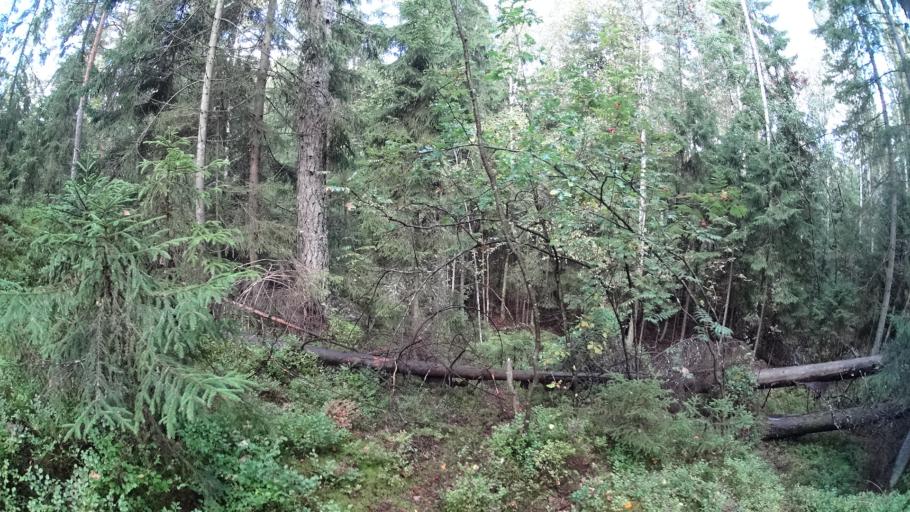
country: FI
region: Uusimaa
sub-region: Helsinki
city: Espoo
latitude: 60.2312
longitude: 24.6841
